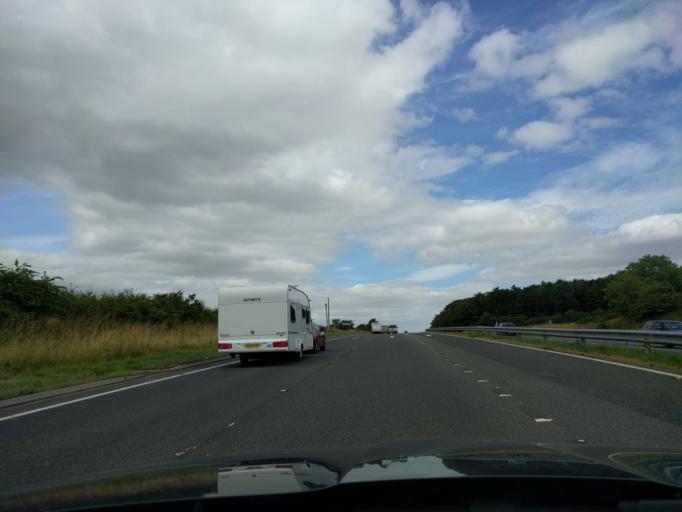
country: GB
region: England
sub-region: Northumberland
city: Alnwick
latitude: 55.3598
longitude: -1.7267
